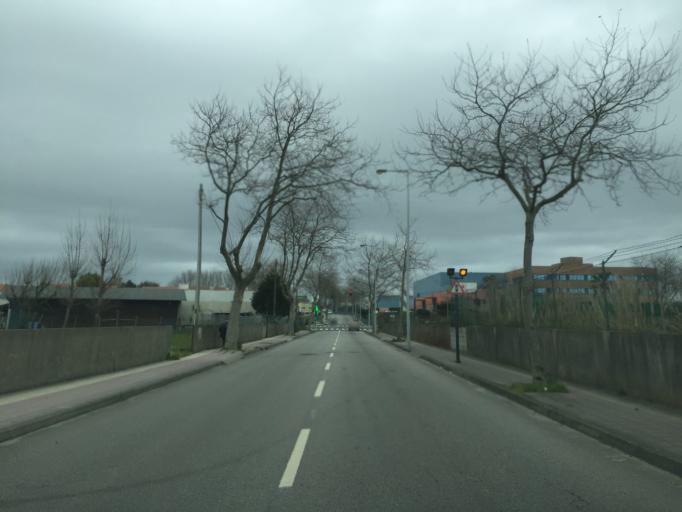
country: PT
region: Porto
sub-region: Matosinhos
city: Santa Cruz do Bispo
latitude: 41.2224
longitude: -8.7055
